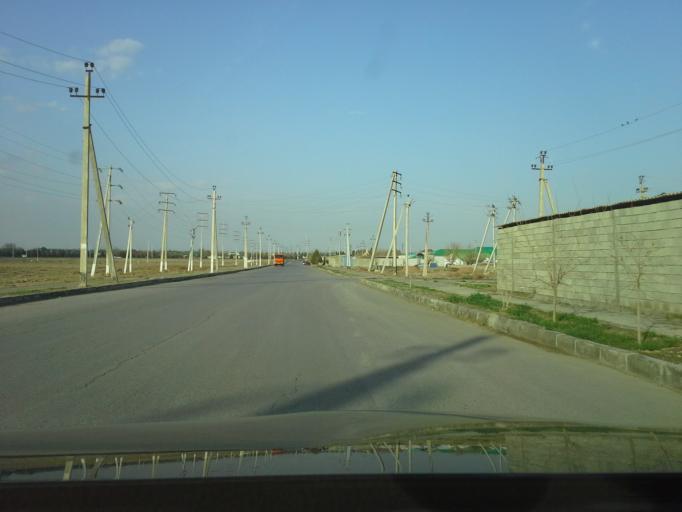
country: TM
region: Ahal
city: Abadan
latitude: 38.0283
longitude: 58.2233
